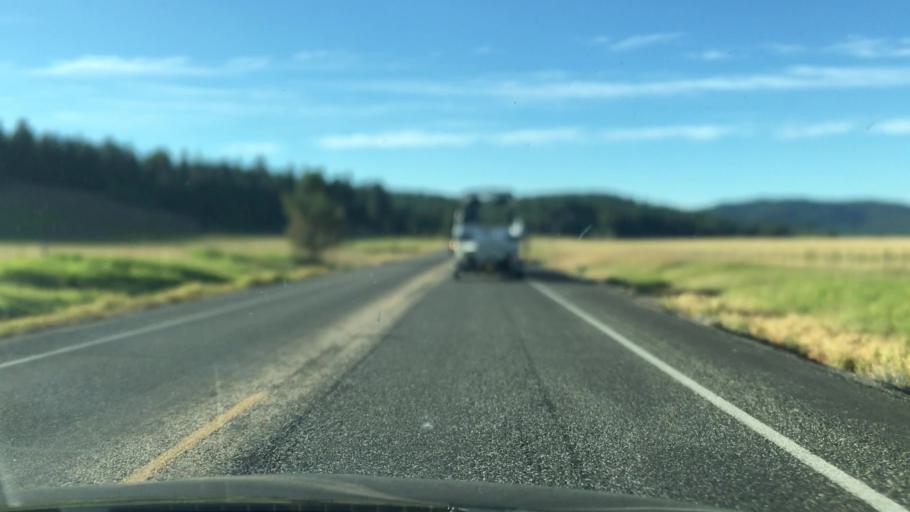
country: US
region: Idaho
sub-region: Valley County
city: Cascade
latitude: 44.5512
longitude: -116.0274
